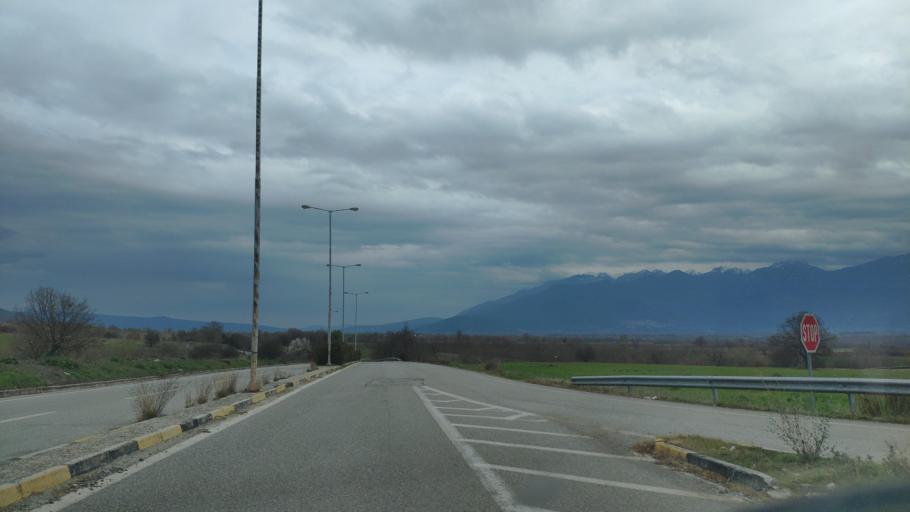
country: GR
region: Central Greece
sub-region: Nomos Fthiotidos
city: Anthili
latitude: 38.7123
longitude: 22.4618
